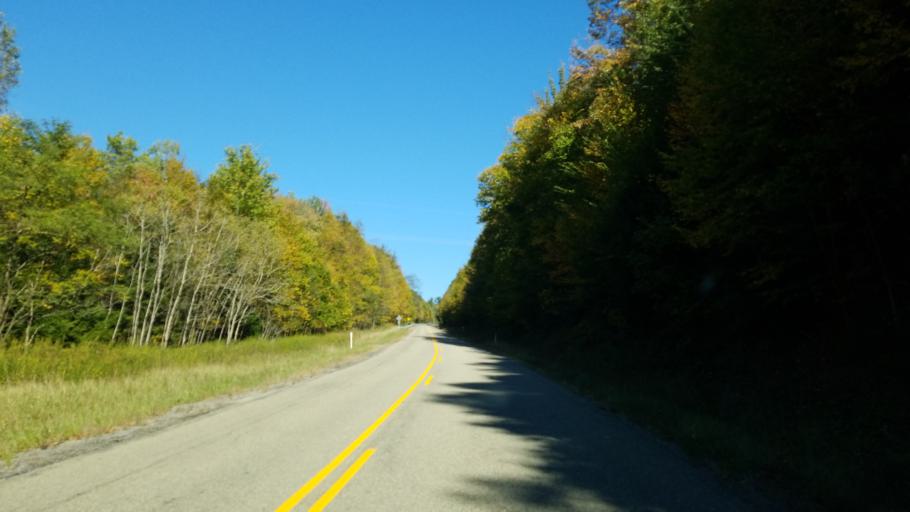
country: US
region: Pennsylvania
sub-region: Clearfield County
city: Shiloh
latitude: 41.2502
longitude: -78.3746
